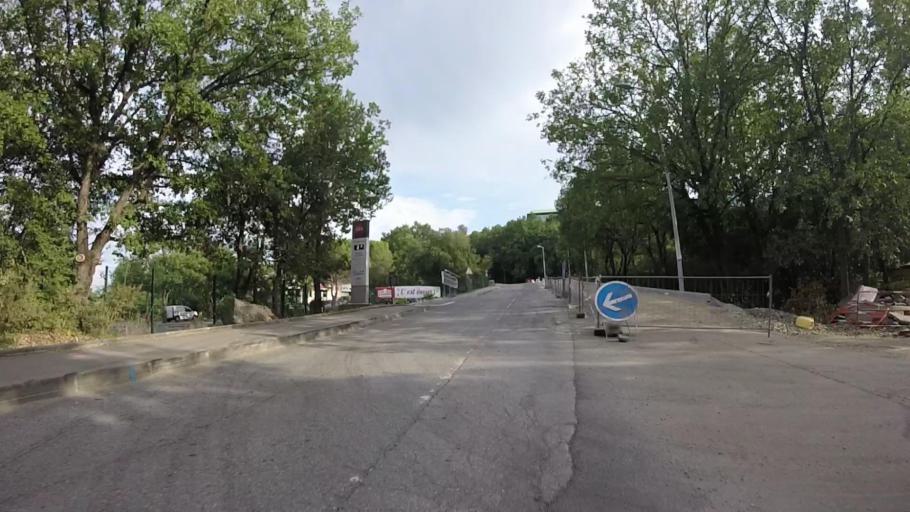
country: FR
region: Provence-Alpes-Cote d'Azur
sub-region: Departement des Alpes-Maritimes
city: Biot
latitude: 43.6205
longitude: 7.0556
